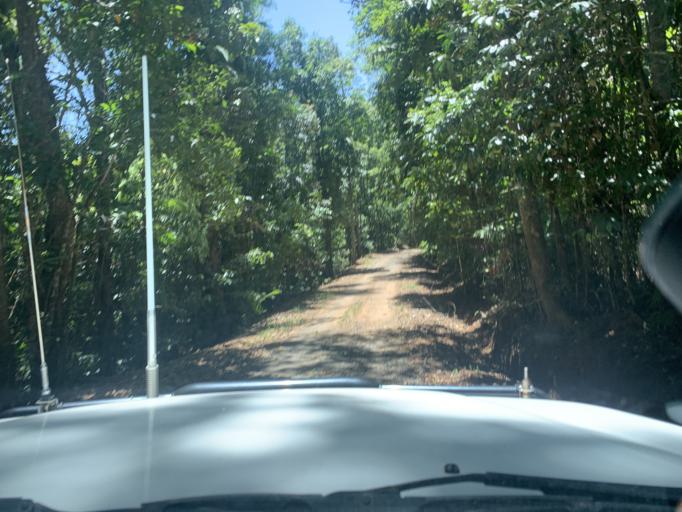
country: AU
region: Queensland
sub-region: Cairns
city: Woree
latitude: -16.9756
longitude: 145.6506
